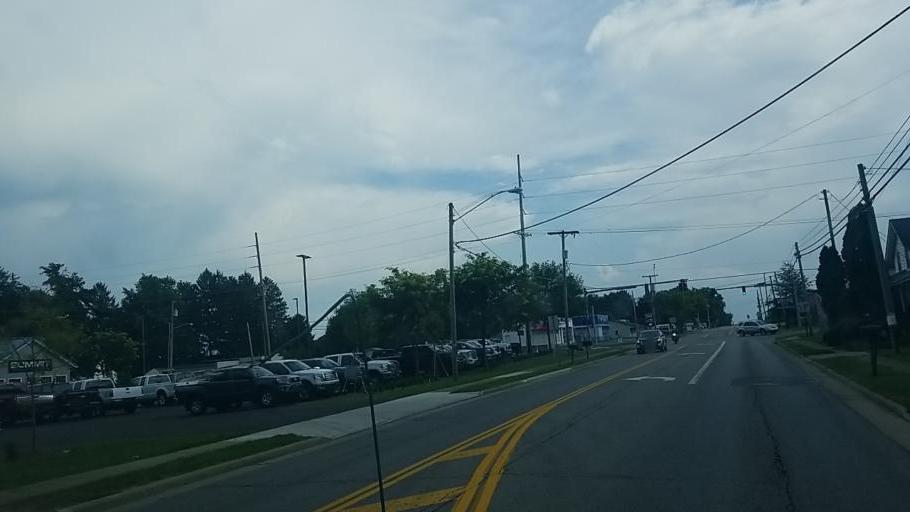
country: US
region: Ohio
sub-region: Wayne County
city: Wooster
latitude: 40.8585
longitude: -81.9246
